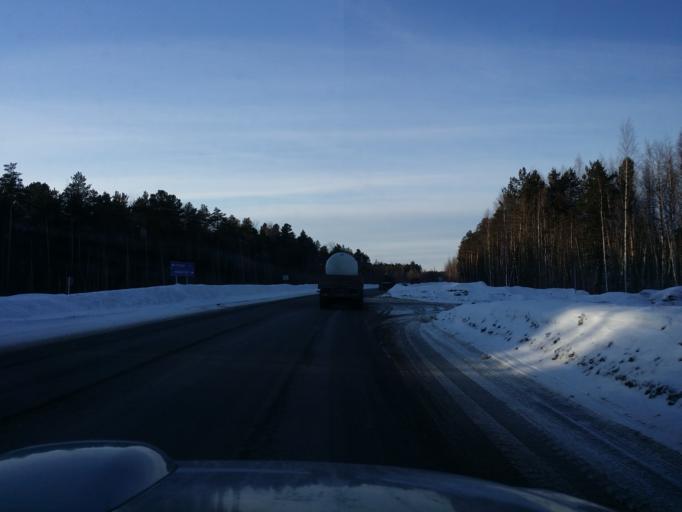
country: RU
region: Khanty-Mansiyskiy Avtonomnyy Okrug
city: Izluchinsk
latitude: 60.9375
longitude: 76.8640
